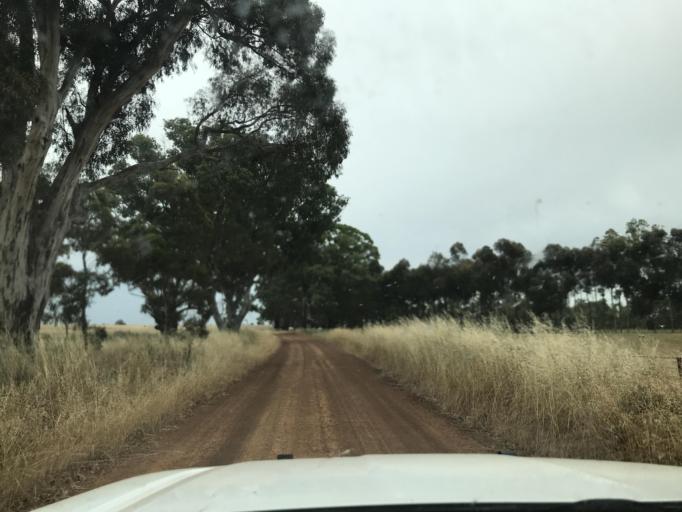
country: AU
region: Victoria
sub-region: Horsham
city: Horsham
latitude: -37.0651
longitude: 141.6571
